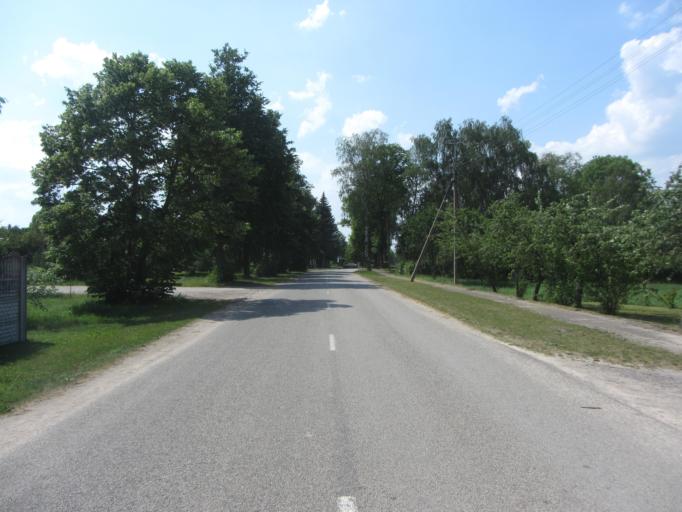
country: LT
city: Lazdijai
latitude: 54.2947
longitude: 23.5549
